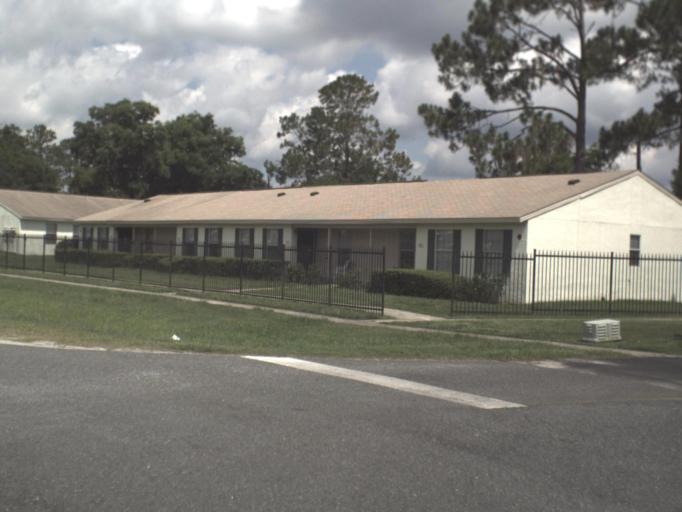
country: US
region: Florida
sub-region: Union County
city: Lake Butler
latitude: 30.0177
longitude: -82.3503
